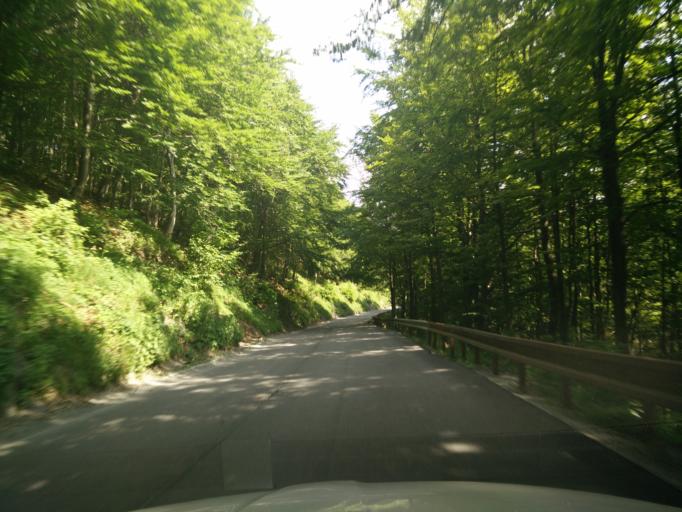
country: SK
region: Zilinsky
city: Rajec
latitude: 48.9556
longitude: 18.6180
